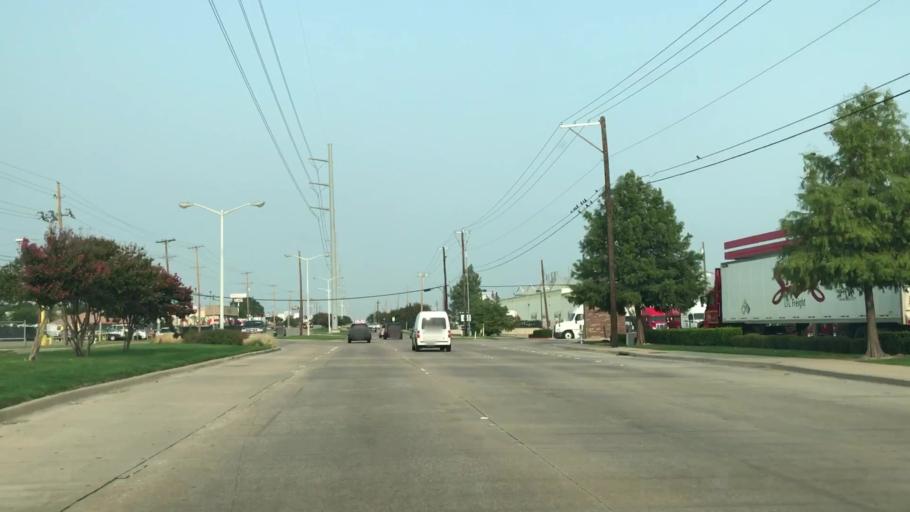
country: US
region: Texas
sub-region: Dallas County
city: Richardson
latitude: 32.9090
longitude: -96.6929
